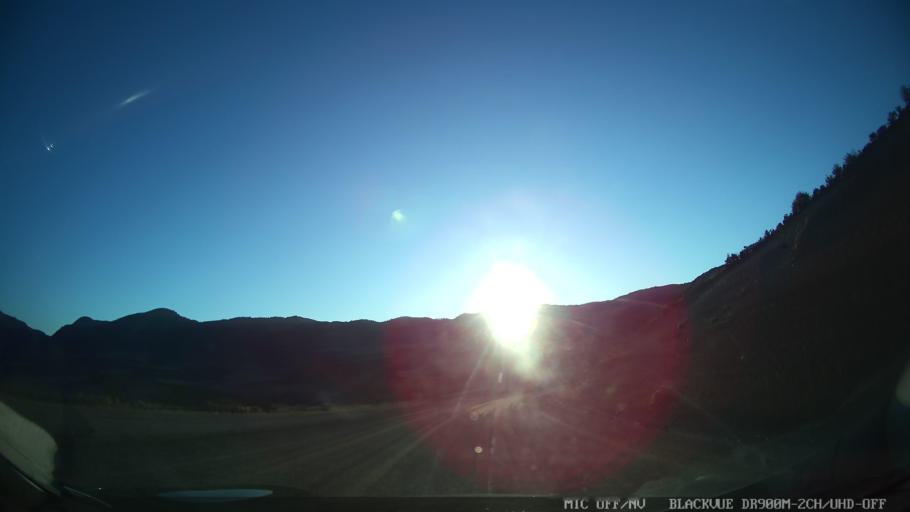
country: US
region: Colorado
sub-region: Grand County
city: Kremmling
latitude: 39.9669
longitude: -106.5181
